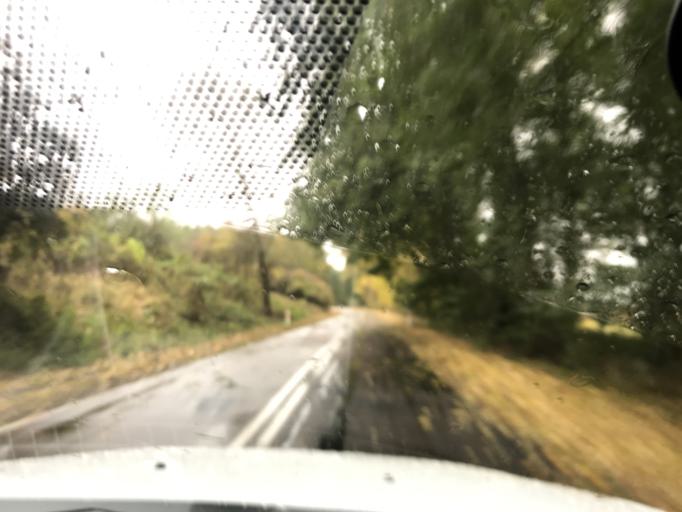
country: DE
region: Brandenburg
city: Neulewin
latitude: 52.7783
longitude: 14.2967
